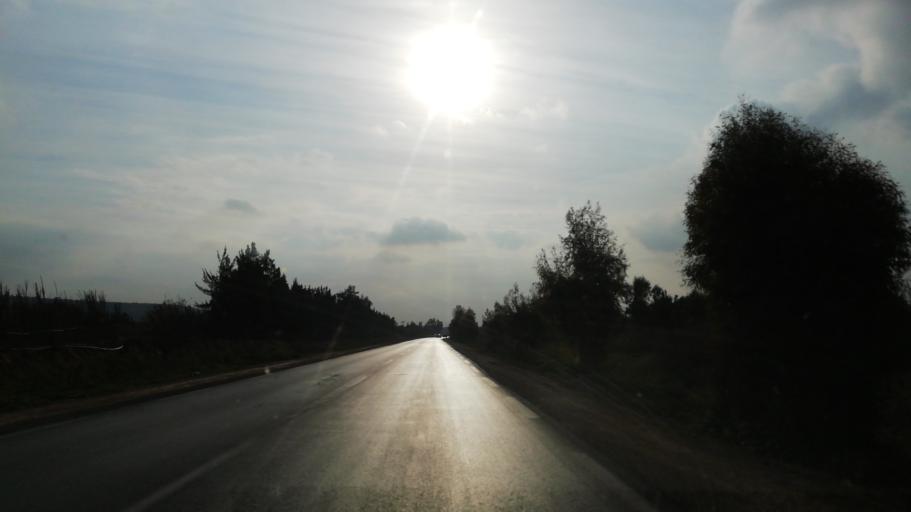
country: DZ
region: Mostaganem
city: Mostaganem
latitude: 35.8425
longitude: 0.0661
